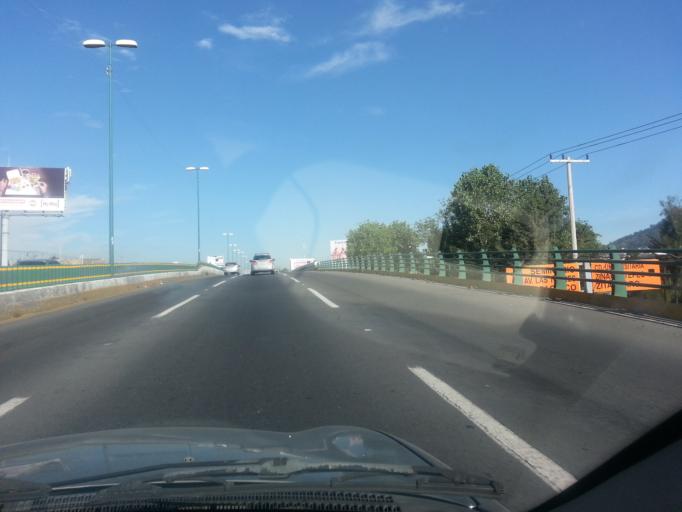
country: MX
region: Mexico
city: San Buenaventura
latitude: 19.2746
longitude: -99.6676
